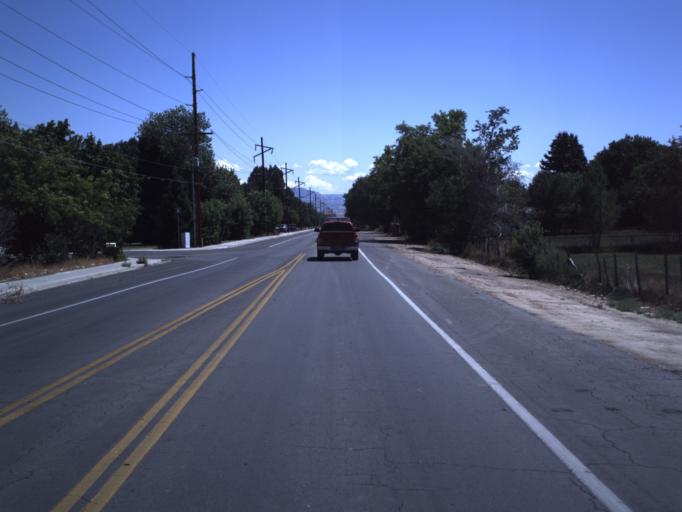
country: US
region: Utah
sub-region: Uintah County
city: Maeser
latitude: 40.4626
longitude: -109.5751
